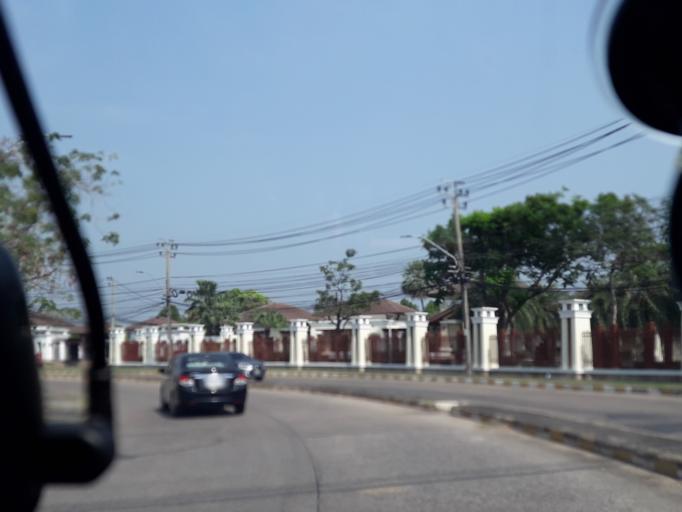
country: TH
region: Bangkok
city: Khlong Sam Wa
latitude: 13.8532
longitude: 100.7070
